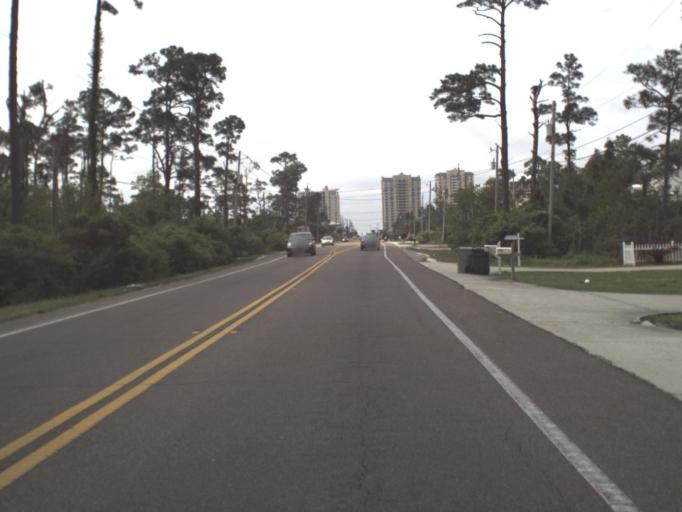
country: US
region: Alabama
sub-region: Baldwin County
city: Orange Beach
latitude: 30.3063
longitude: -87.4275
